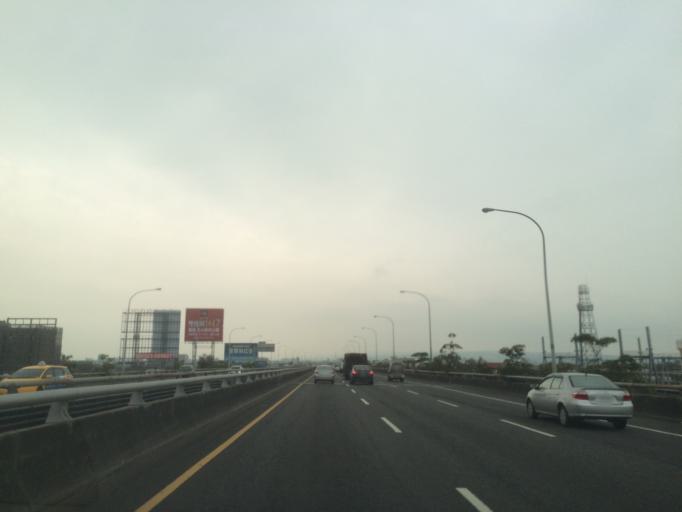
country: TW
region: Taiwan
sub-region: Taichung City
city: Taichung
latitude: 24.1429
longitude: 120.6228
